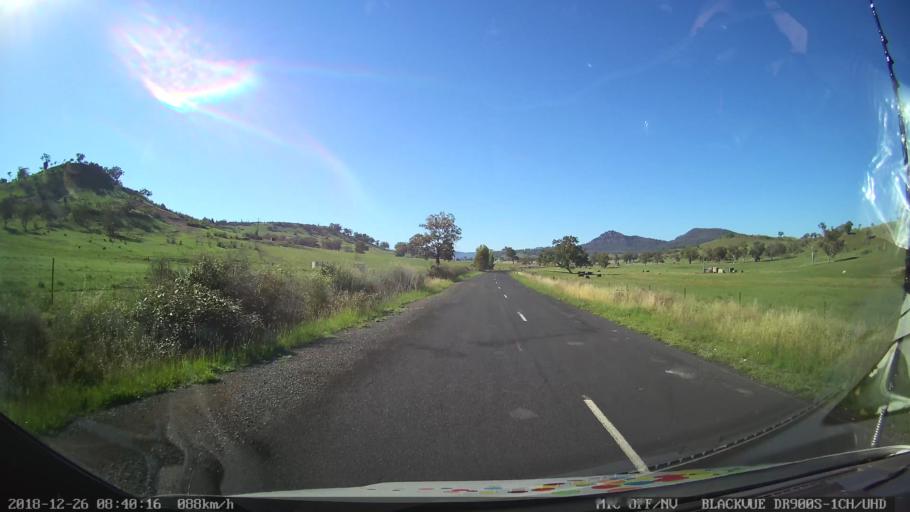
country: AU
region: New South Wales
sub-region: Mid-Western Regional
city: Kandos
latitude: -32.4647
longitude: 150.0762
